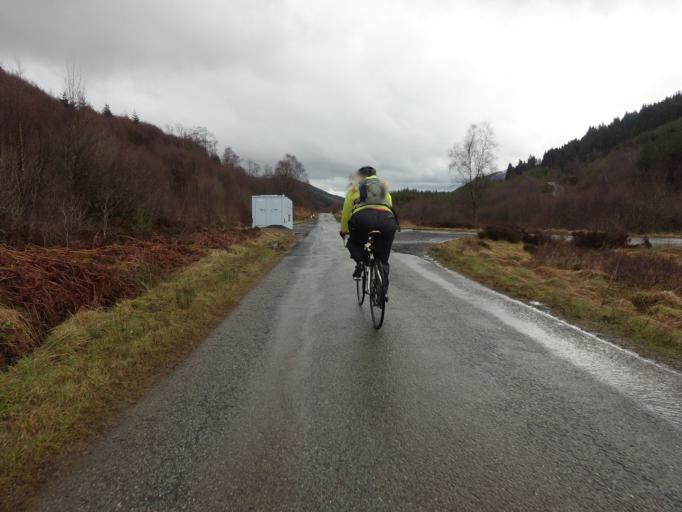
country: GB
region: Scotland
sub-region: West Dunbartonshire
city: Balloch
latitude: 56.2420
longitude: -4.5710
